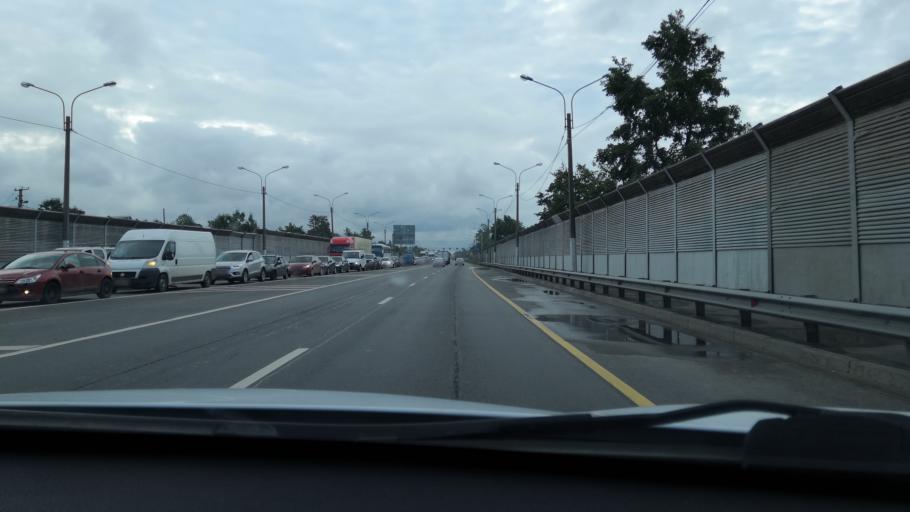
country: RU
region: St.-Petersburg
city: Kolpino
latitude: 59.7021
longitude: 30.5820
